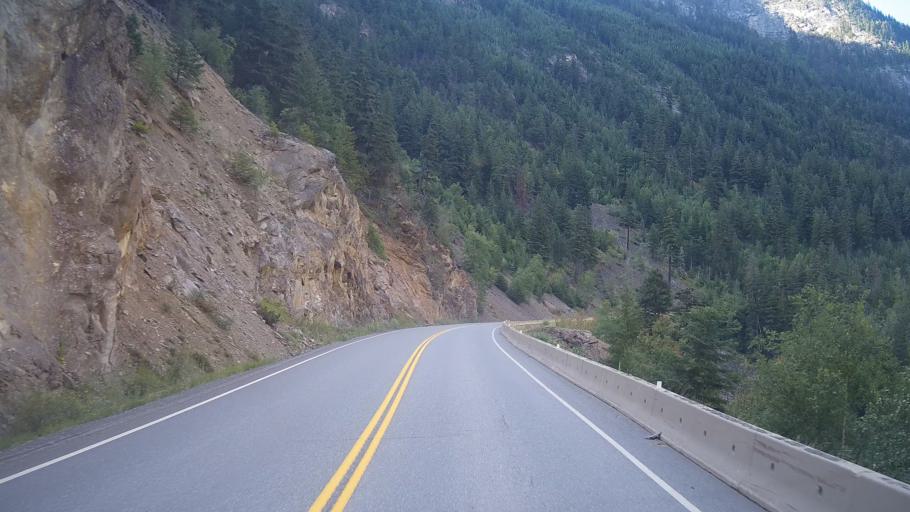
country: CA
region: British Columbia
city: Lillooet
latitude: 50.6446
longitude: -122.0696
